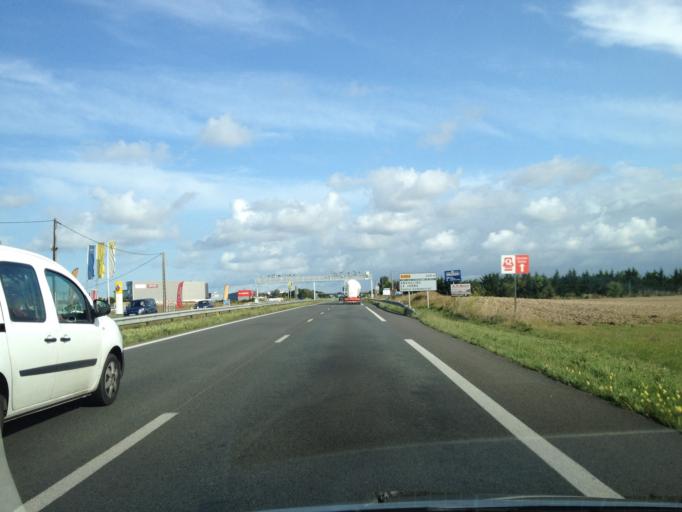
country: FR
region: Poitou-Charentes
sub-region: Departement de la Charente-Maritime
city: Angoulins
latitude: 46.0993
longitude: -1.0916
